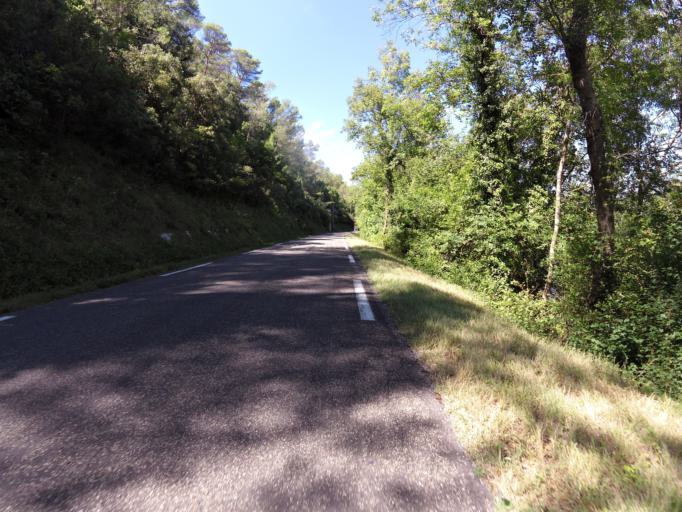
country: FR
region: Languedoc-Roussillon
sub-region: Departement du Gard
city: Sommieres
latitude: 43.8237
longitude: 4.0666
